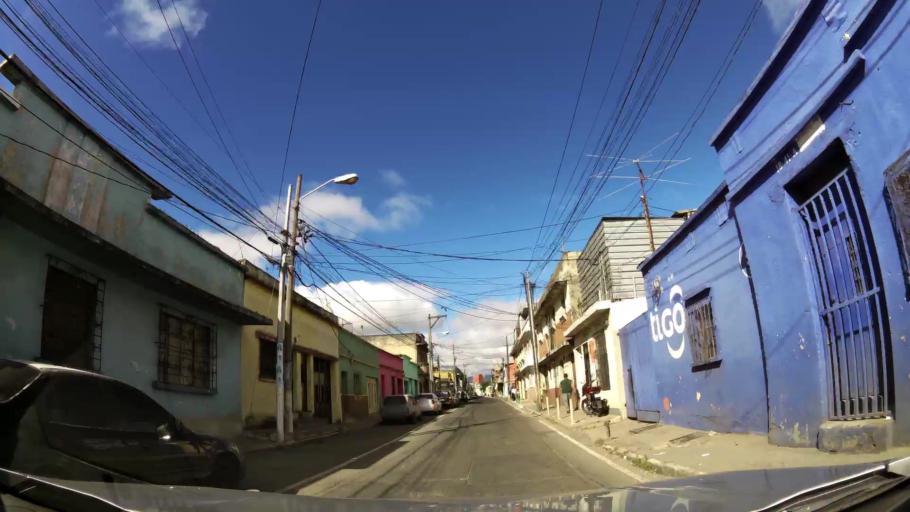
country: GT
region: Guatemala
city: Guatemala City
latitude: 14.6188
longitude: -90.5069
